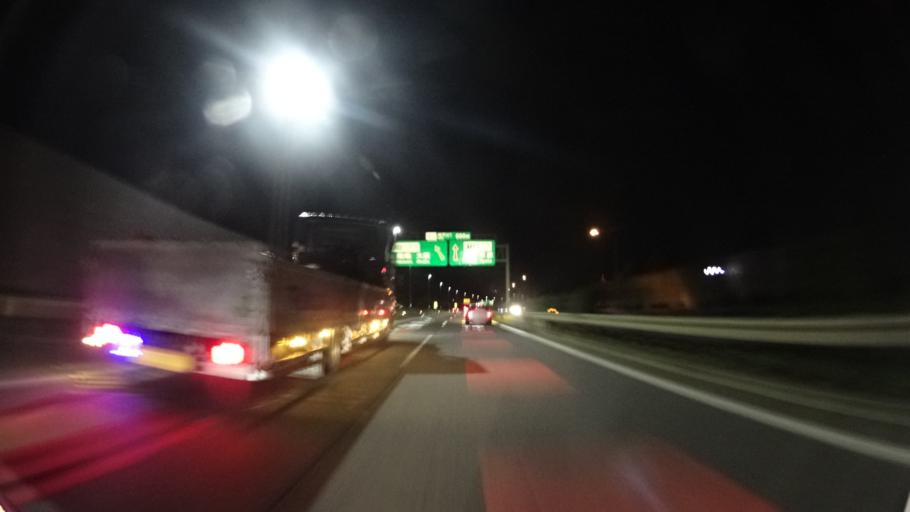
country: JP
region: Hyogo
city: Sandacho
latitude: 34.8471
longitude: 135.2087
